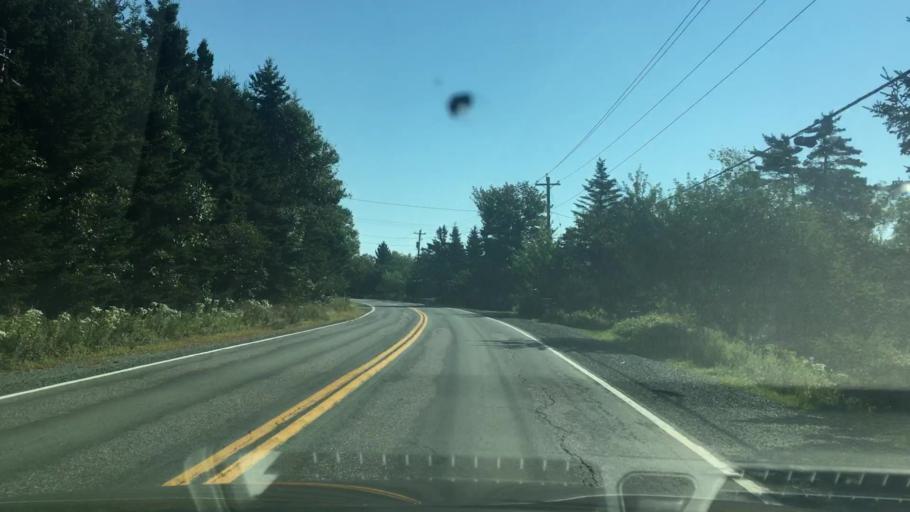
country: CA
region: Nova Scotia
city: Cole Harbour
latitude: 44.7765
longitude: -63.0698
